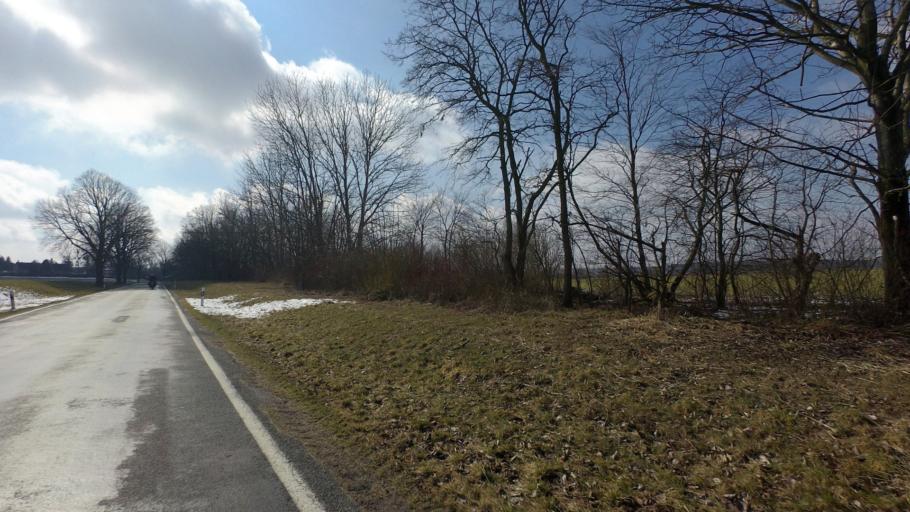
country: DE
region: Brandenburg
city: Werneuchen
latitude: 52.6878
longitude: 13.7283
